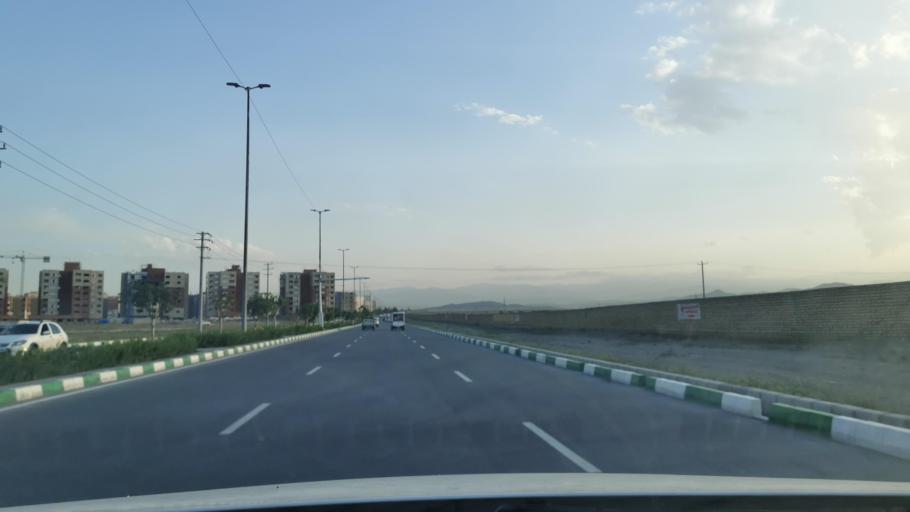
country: IR
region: Razavi Khorasan
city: Mashhad
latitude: 36.3969
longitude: 59.4753
